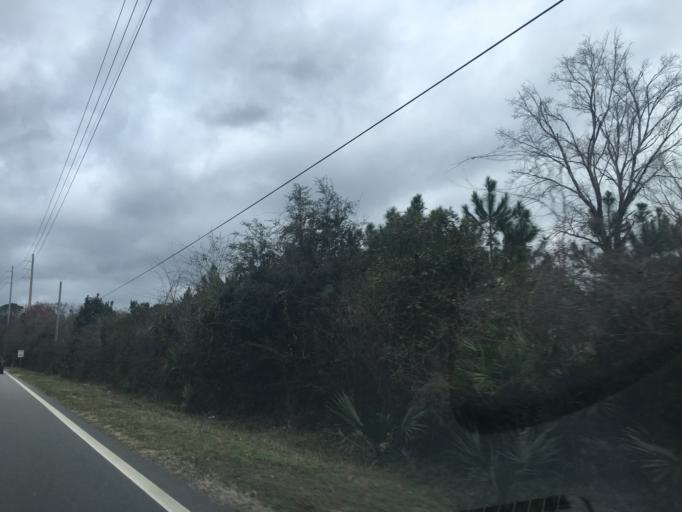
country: US
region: Florida
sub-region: Saint Johns County
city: Villano Beach
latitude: 30.0024
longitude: -81.4145
